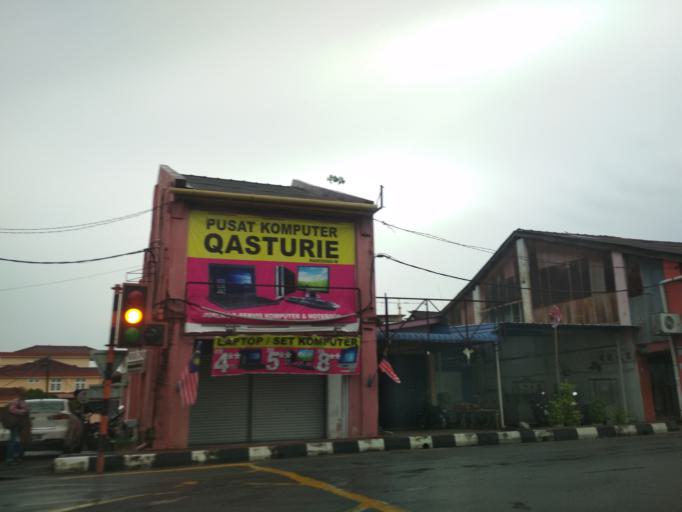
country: MY
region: Perlis
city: Kangar
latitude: 6.4386
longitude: 100.1956
